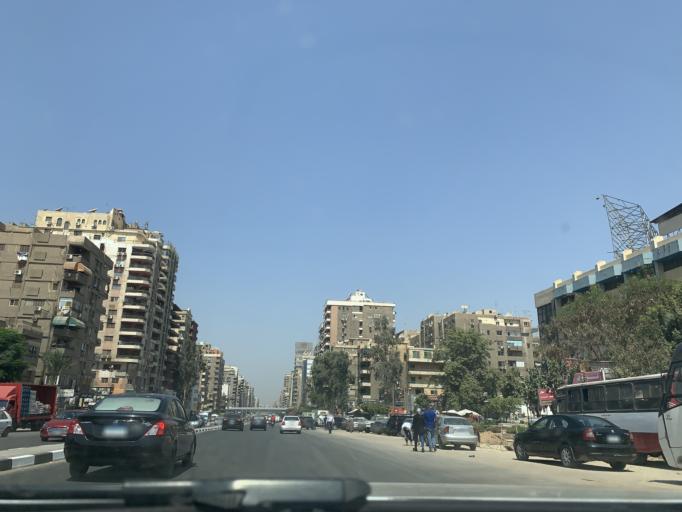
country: EG
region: Muhafazat al Qahirah
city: Cairo
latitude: 30.0503
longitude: 31.3469
